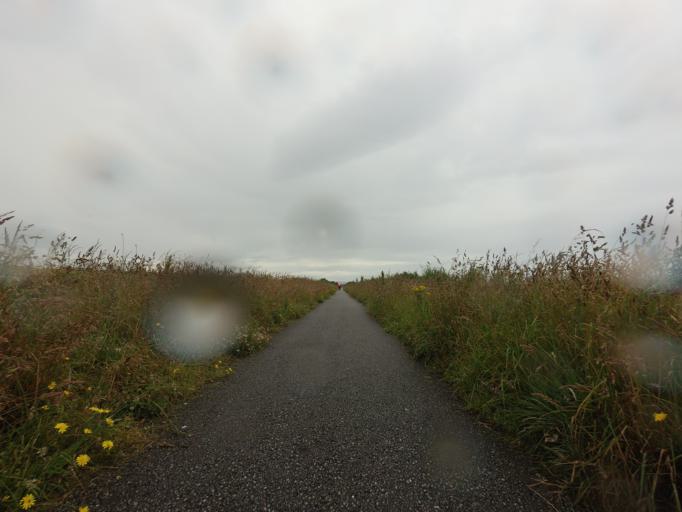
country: GB
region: Scotland
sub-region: Moray
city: Findochty
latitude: 57.6938
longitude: -2.9059
